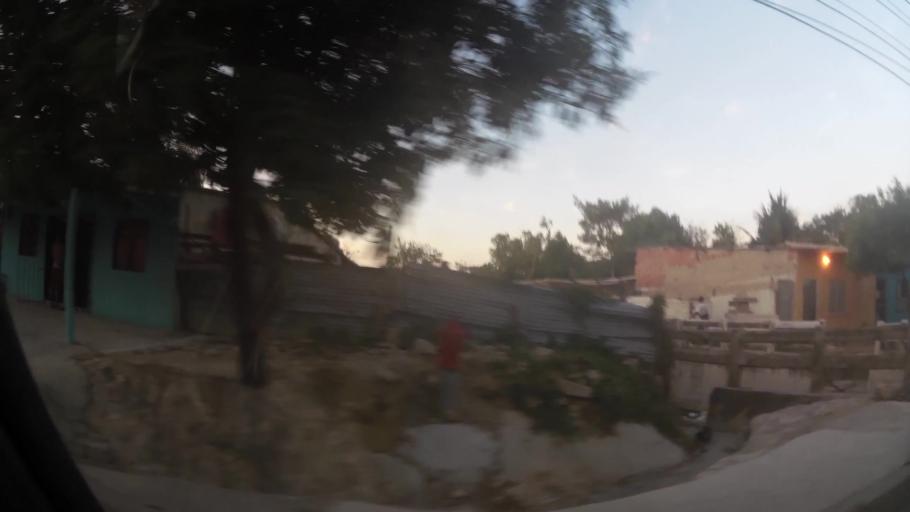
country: CO
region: Atlantico
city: Barranquilla
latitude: 10.9575
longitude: -74.8323
